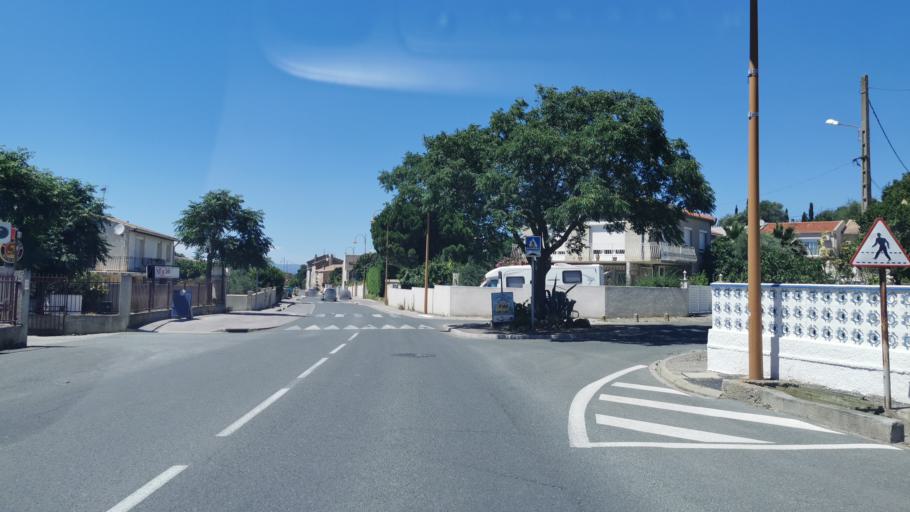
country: FR
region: Languedoc-Roussillon
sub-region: Departement de l'Aude
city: Fleury
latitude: 43.2335
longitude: 3.1233
